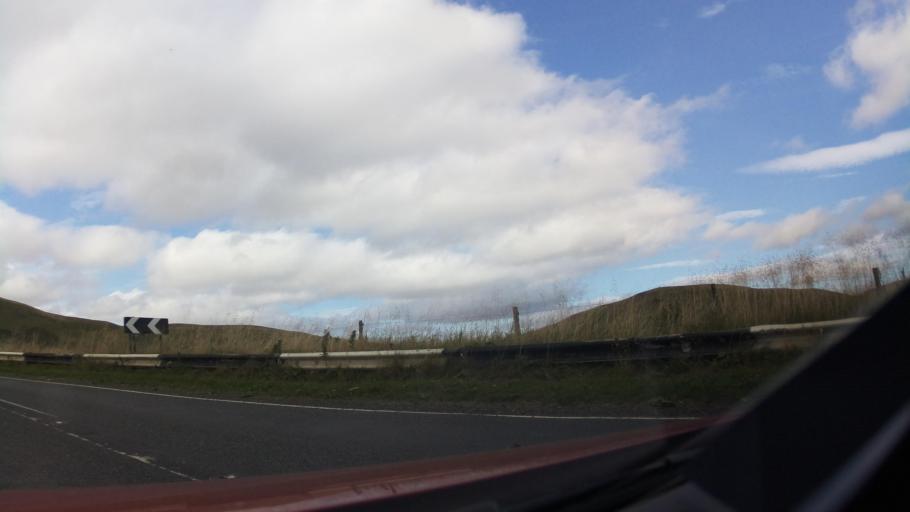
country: GB
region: Scotland
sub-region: Dumfries and Galloway
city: Moffat
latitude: 55.3971
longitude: -3.4817
